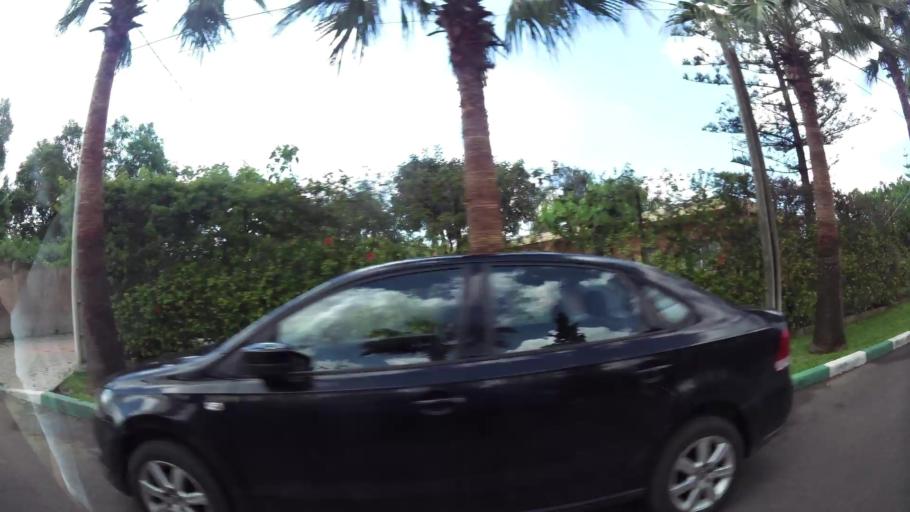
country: MA
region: Grand Casablanca
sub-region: Mediouna
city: Mediouna
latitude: 33.3862
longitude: -7.5410
